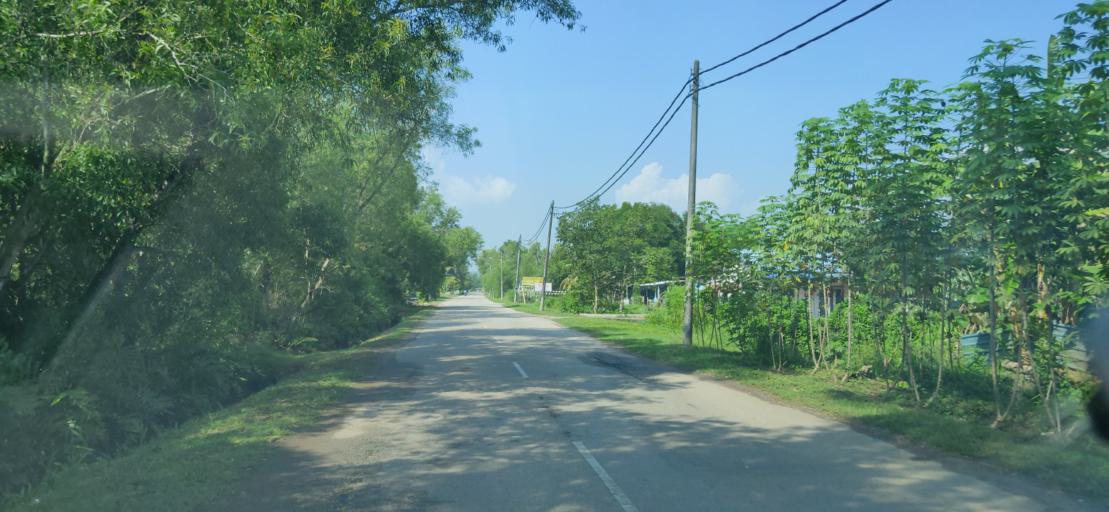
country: MY
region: Kedah
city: Sungai Petani
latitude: 5.6675
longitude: 100.4611
